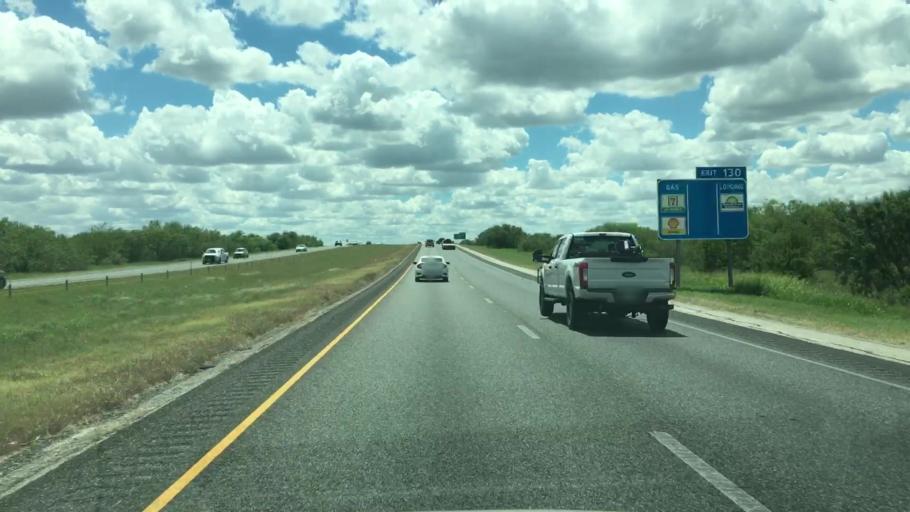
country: US
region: Texas
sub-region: Bexar County
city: Elmendorf
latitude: 29.2940
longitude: -98.3953
